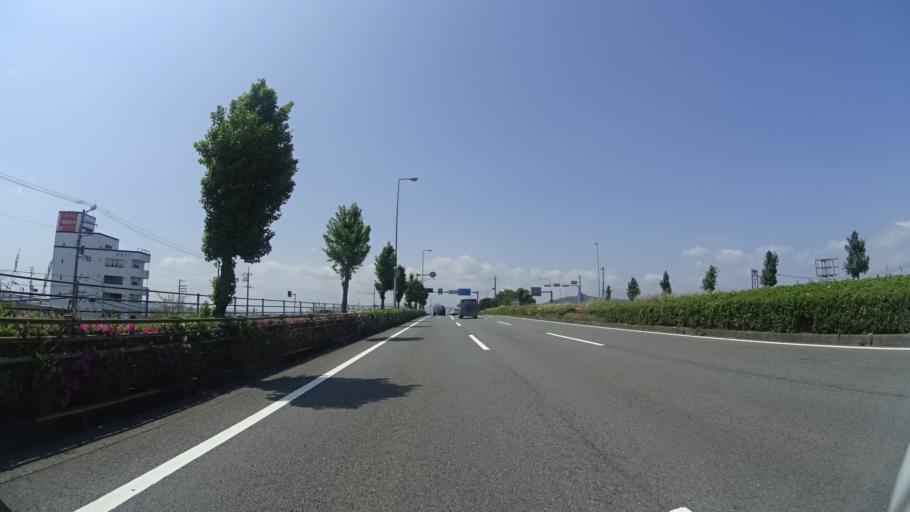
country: JP
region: Tokushima
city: Tokushima-shi
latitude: 34.0951
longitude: 134.5719
